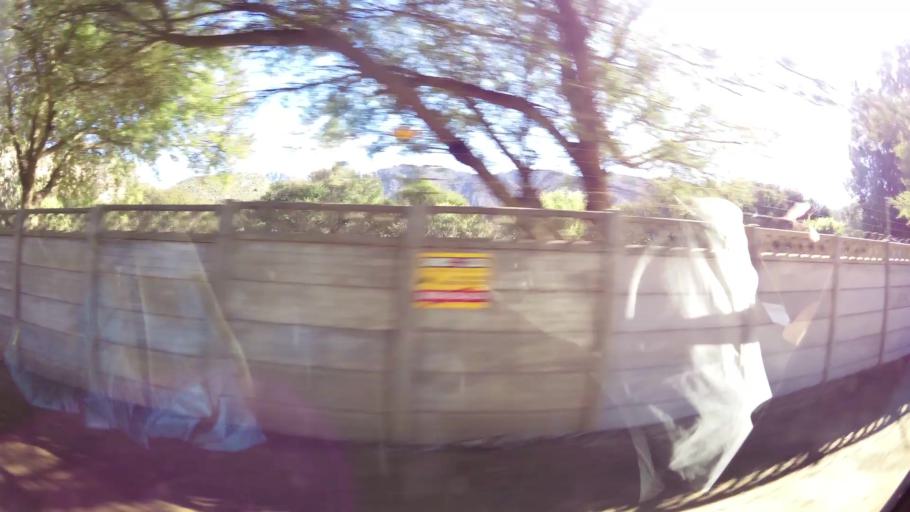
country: ZA
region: Western Cape
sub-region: Cape Winelands District Municipality
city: Ashton
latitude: -33.7865
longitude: 20.1142
